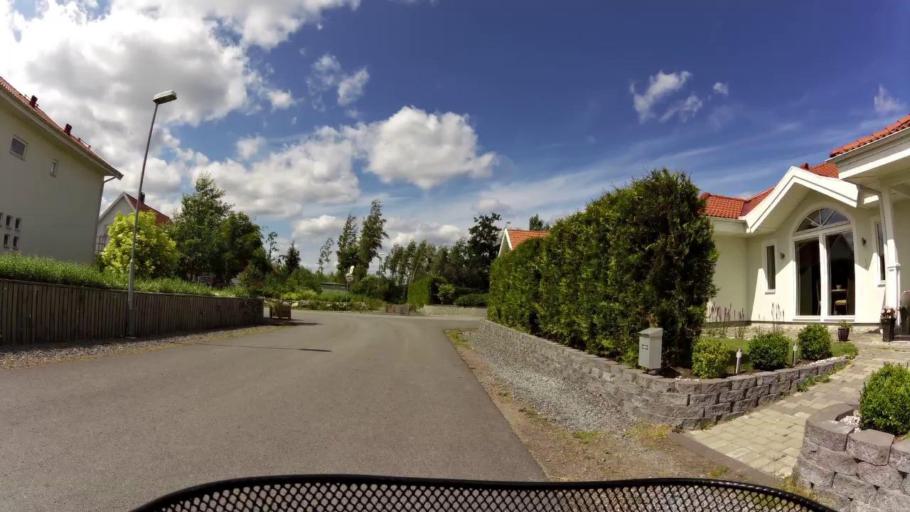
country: SE
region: OEstergoetland
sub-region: Linkopings Kommun
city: Ekangen
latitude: 58.4762
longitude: 15.6377
